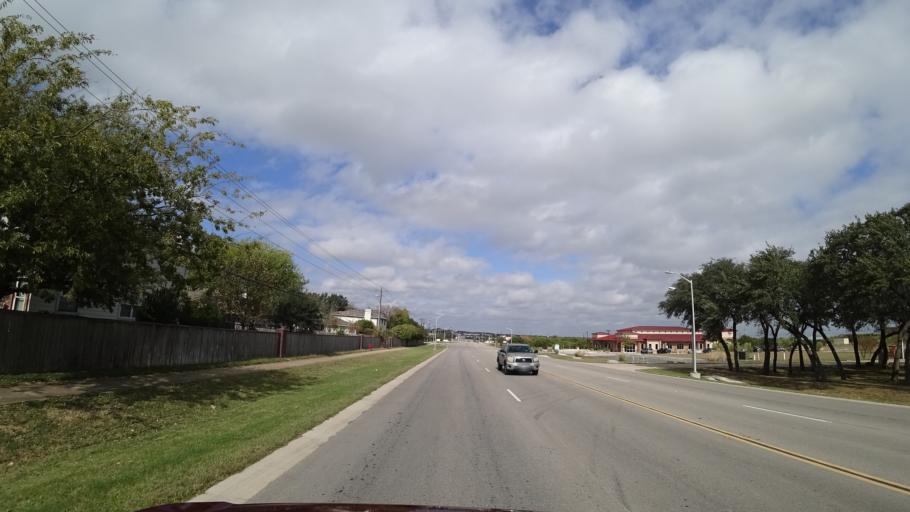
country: US
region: Texas
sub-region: Williamson County
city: Cedar Park
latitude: 30.5267
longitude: -97.8438
